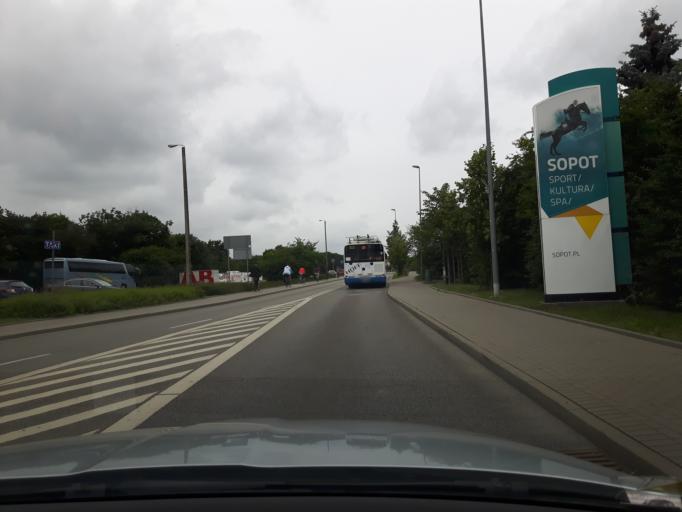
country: PL
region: Pomeranian Voivodeship
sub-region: Sopot
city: Sopot
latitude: 54.4264
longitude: 18.5762
